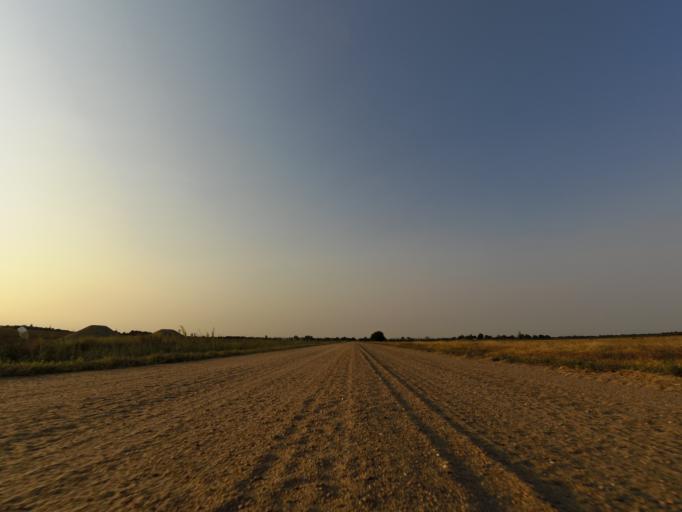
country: US
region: Kansas
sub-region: Reno County
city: South Hutchinson
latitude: 37.9755
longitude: -97.9957
